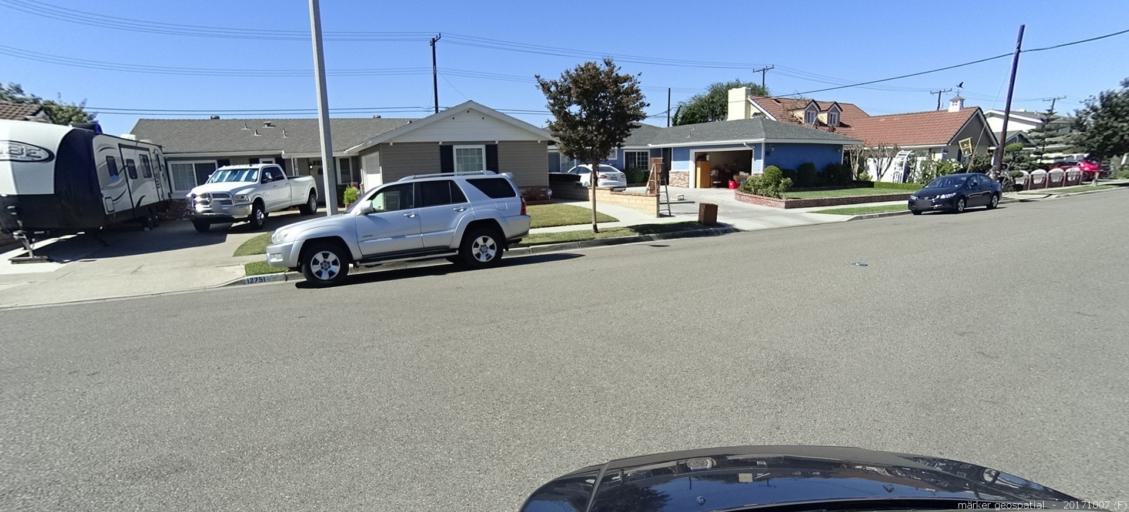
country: US
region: California
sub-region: Orange County
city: Westminster
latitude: 33.7773
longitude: -118.0420
